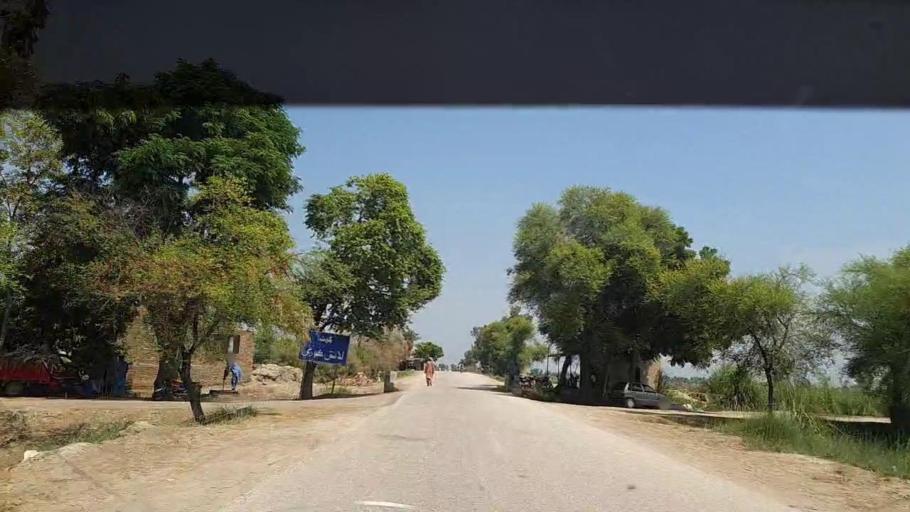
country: PK
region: Sindh
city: Thul
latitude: 28.1111
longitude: 68.8078
